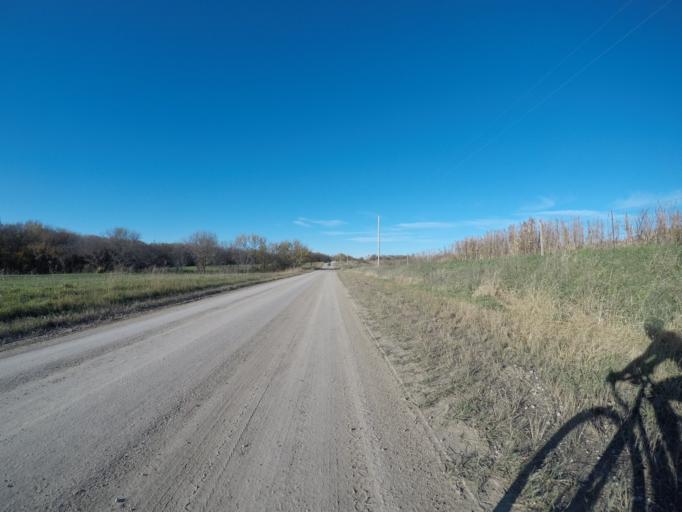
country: US
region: Kansas
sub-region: Riley County
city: Fort Riley North
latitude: 39.2725
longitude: -96.7844
